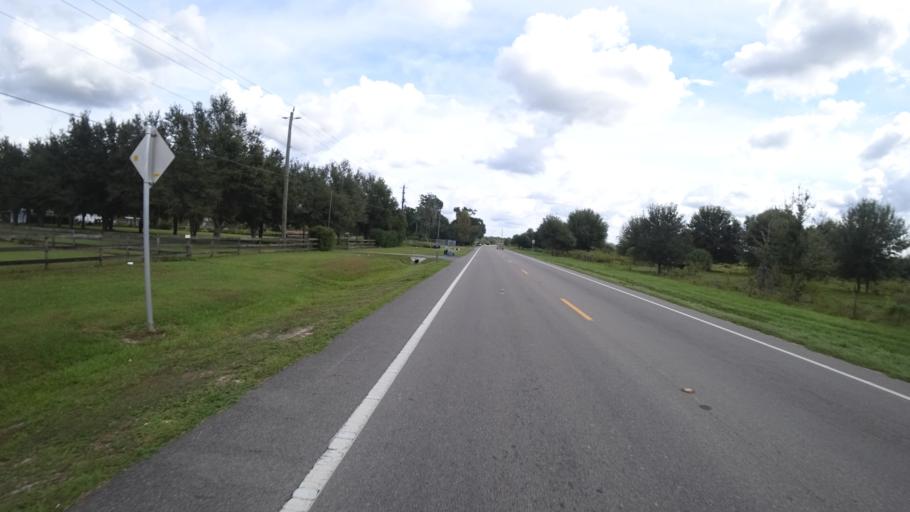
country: US
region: Florida
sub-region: Manatee County
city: Ellenton
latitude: 27.5877
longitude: -82.4216
